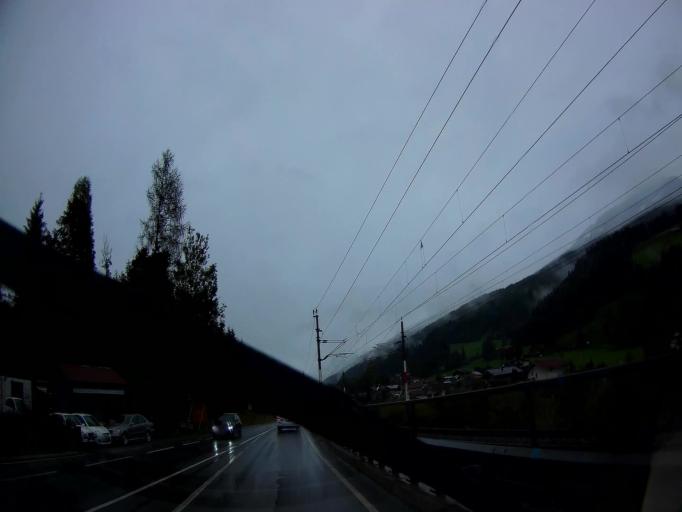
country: AT
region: Salzburg
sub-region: Politischer Bezirk Zell am See
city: Bruck an der Grossglocknerstrasse
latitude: 47.2880
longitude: 12.8838
